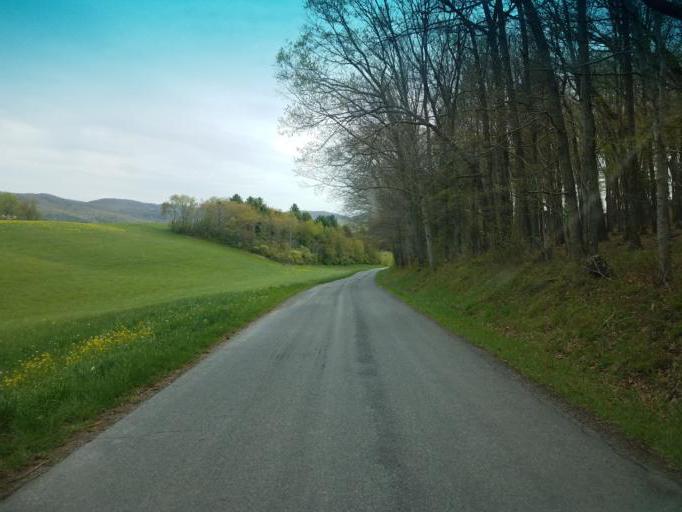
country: US
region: Virginia
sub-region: Smyth County
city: Marion
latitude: 36.7652
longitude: -81.4575
